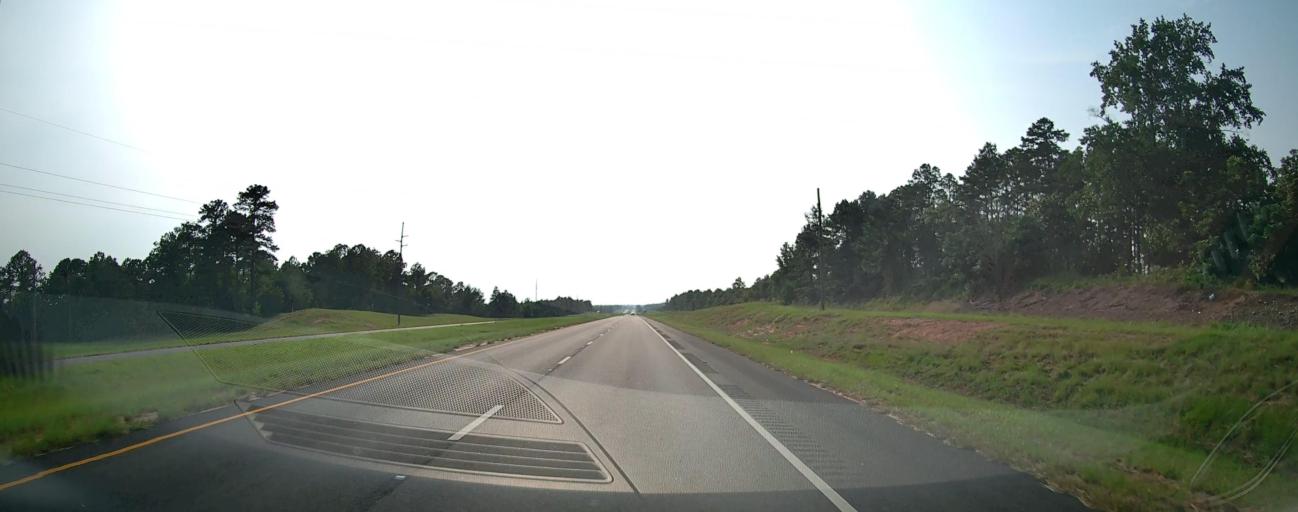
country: US
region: Georgia
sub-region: Taylor County
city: Butler
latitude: 32.5797
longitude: -84.3201
